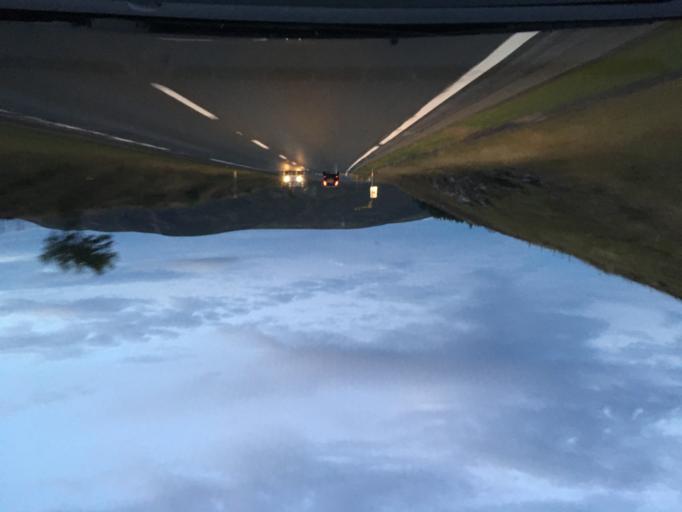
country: GB
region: Scotland
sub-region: Highland
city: Kingussie
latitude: 56.8412
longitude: -4.2357
